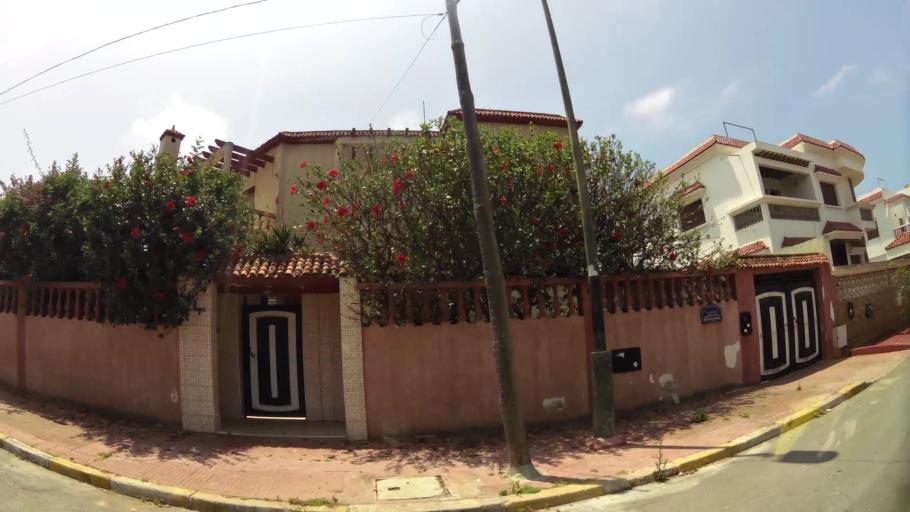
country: MA
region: Rabat-Sale-Zemmour-Zaer
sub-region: Skhirate-Temara
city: Temara
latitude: 33.9705
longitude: -6.9020
